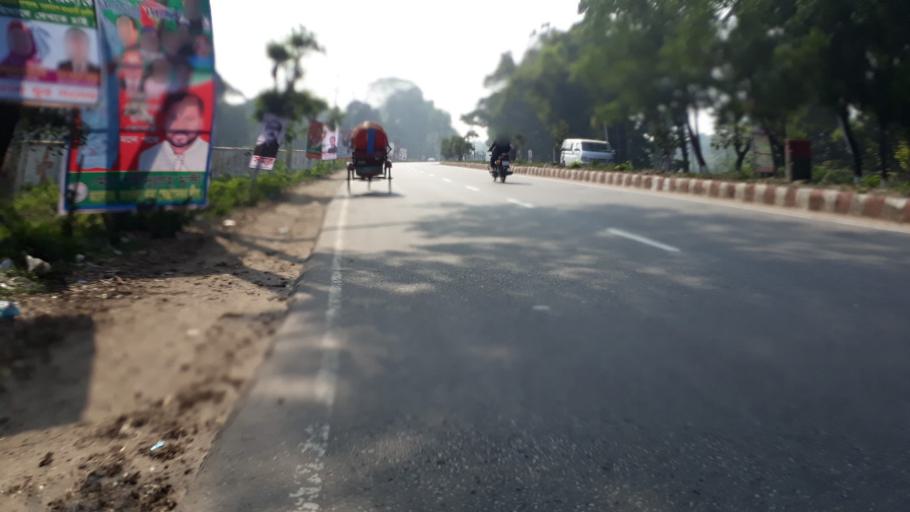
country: BD
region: Dhaka
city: Tungi
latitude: 23.8756
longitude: 90.2735
